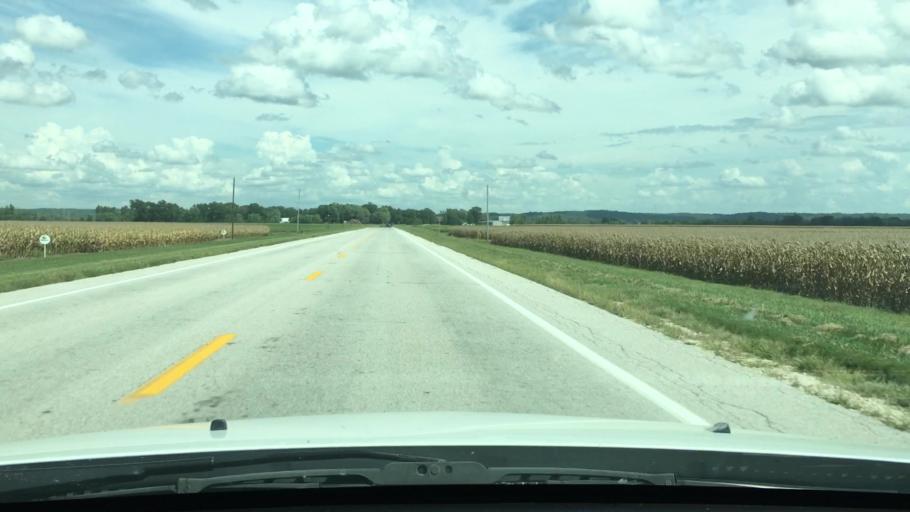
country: US
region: Missouri
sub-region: Pike County
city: Louisiana
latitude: 39.4793
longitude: -91.0185
